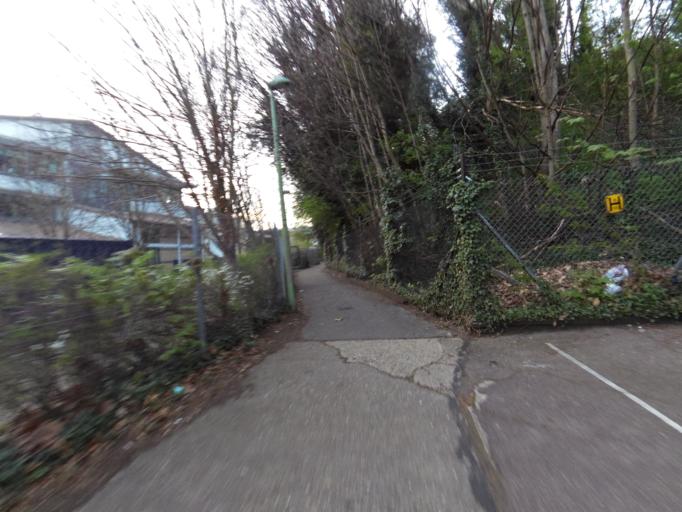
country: GB
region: England
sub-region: Suffolk
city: Ipswich
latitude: 52.0534
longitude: 1.1668
